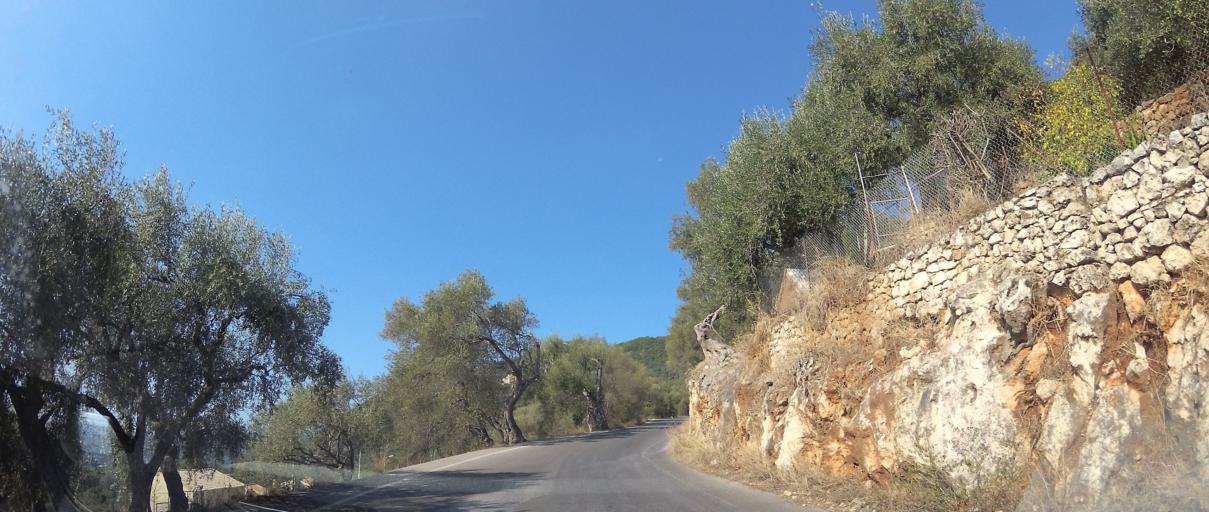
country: GR
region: Ionian Islands
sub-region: Nomos Kerkyras
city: Kontokali
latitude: 39.7163
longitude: 19.8488
